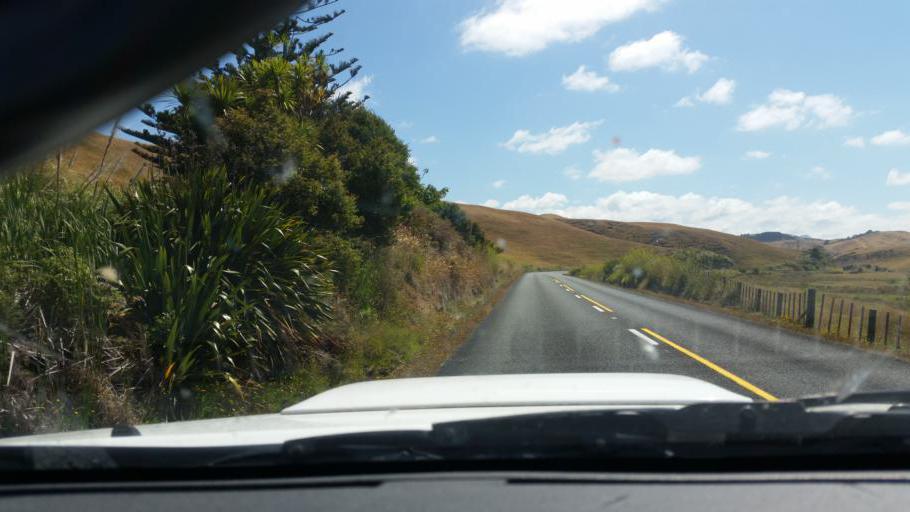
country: NZ
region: Northland
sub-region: Kaipara District
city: Dargaville
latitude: -35.8334
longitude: 173.6621
